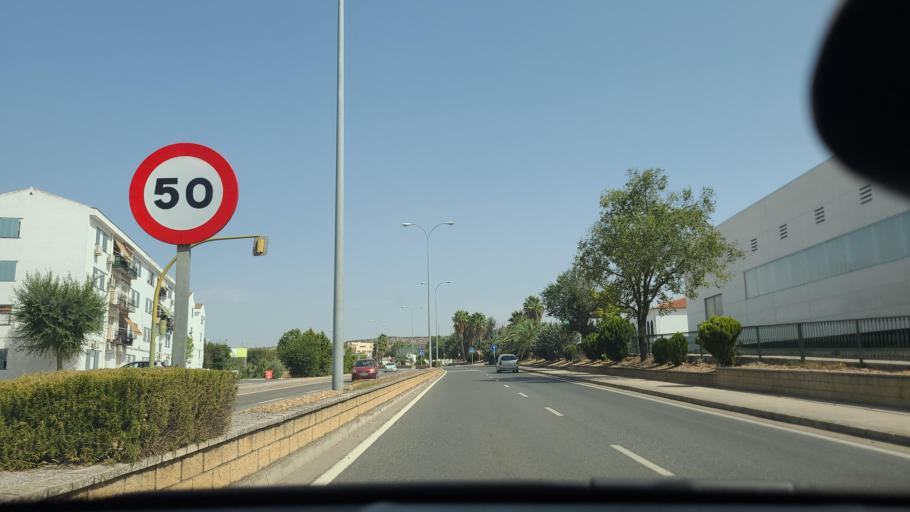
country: ES
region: Extremadura
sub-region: Provincia de Badajoz
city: Zafra
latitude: 38.4259
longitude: -6.4116
